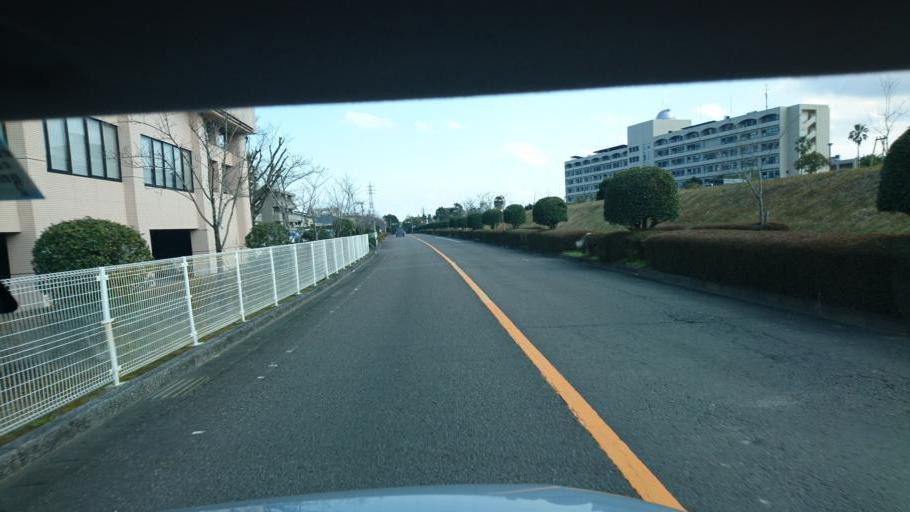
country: JP
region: Miyazaki
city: Miyazaki-shi
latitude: 31.8326
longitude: 131.4120
